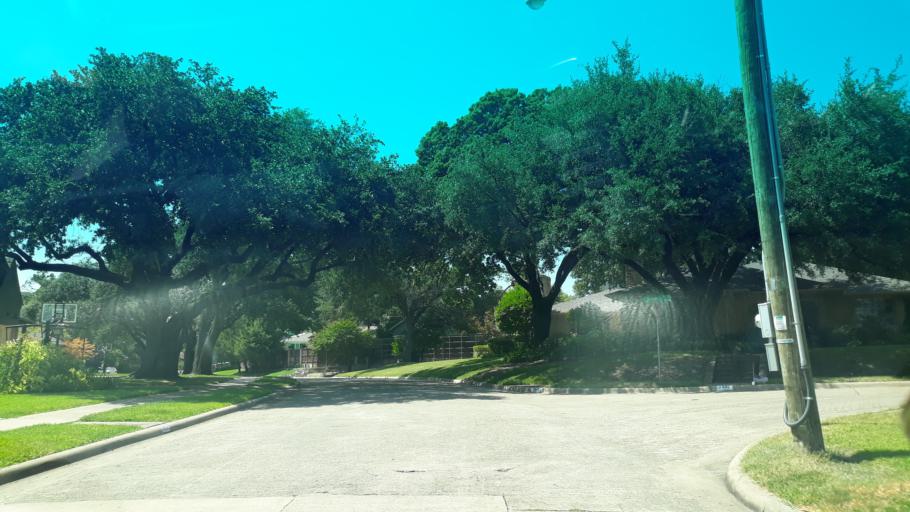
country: US
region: Texas
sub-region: Dallas County
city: Highland Park
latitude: 32.8277
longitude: -96.7416
